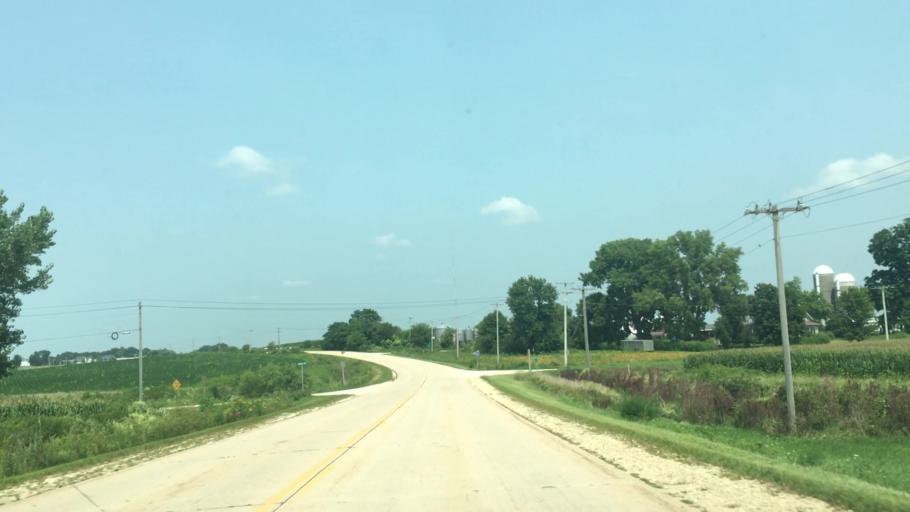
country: US
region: Iowa
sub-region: Fayette County
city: Oelwein
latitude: 42.6638
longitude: -91.8953
